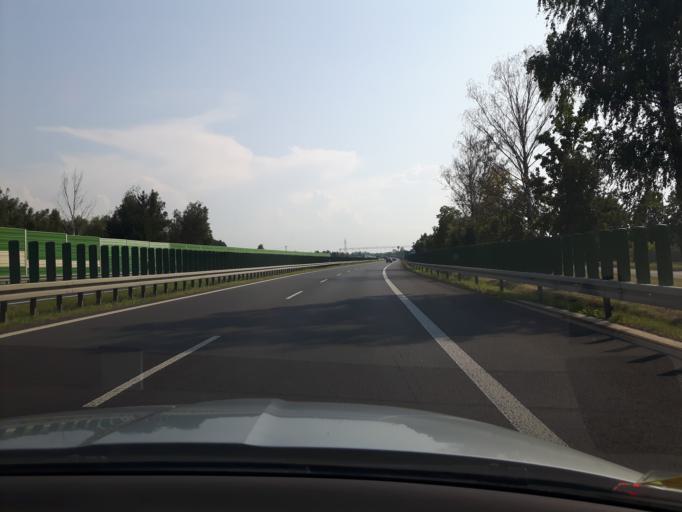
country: PL
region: Masovian Voivodeship
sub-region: Powiat plonski
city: Plonsk
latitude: 52.6231
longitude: 20.3898
